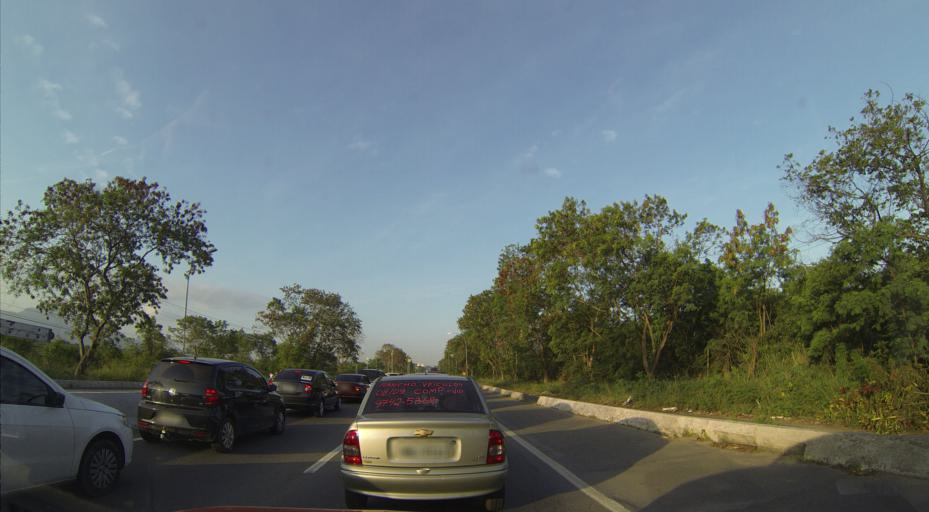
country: BR
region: Espirito Santo
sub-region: Vila Velha
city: Vila Velha
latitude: -20.2497
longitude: -40.2858
